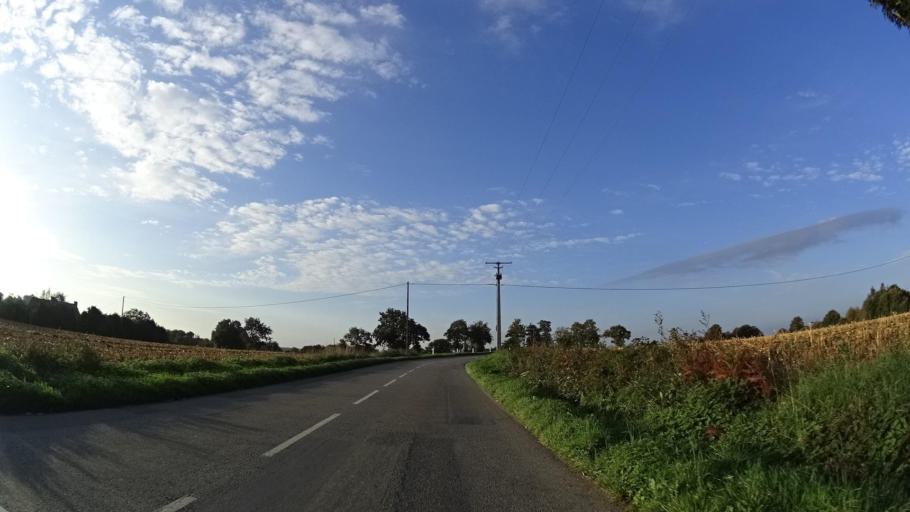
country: FR
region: Brittany
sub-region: Departement des Cotes-d'Armor
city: Plouasne
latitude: 48.2862
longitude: -1.9696
